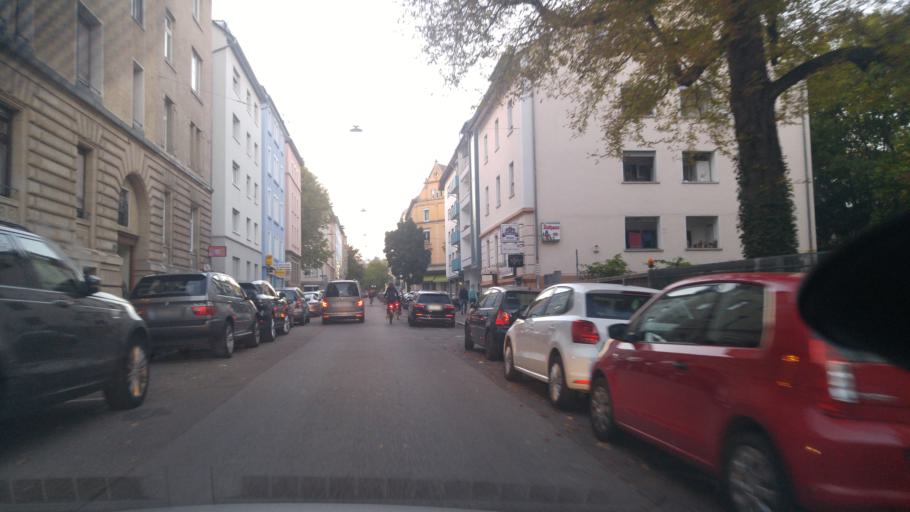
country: DE
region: Baden-Wuerttemberg
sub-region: Regierungsbezirk Stuttgart
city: Stuttgart
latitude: 48.7717
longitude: 9.1611
